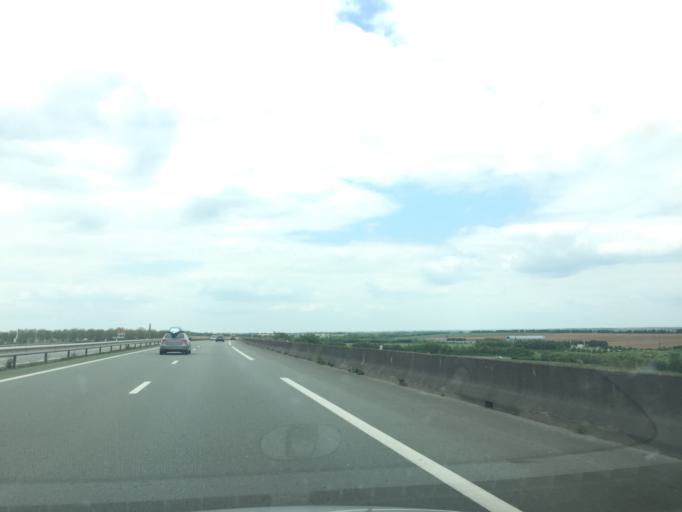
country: FR
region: Poitou-Charentes
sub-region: Departement des Deux-Sevres
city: La Creche
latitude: 46.3497
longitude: -0.3253
